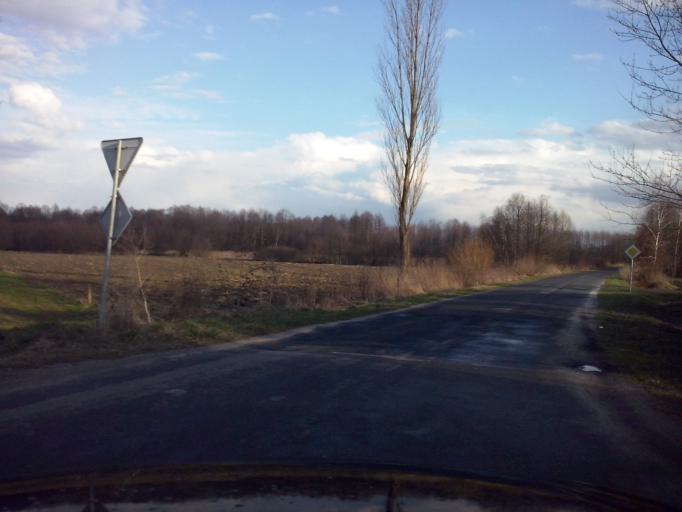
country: PL
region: Lublin Voivodeship
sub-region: Powiat chelmski
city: Ruda-Huta
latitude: 51.1966
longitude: 23.5375
